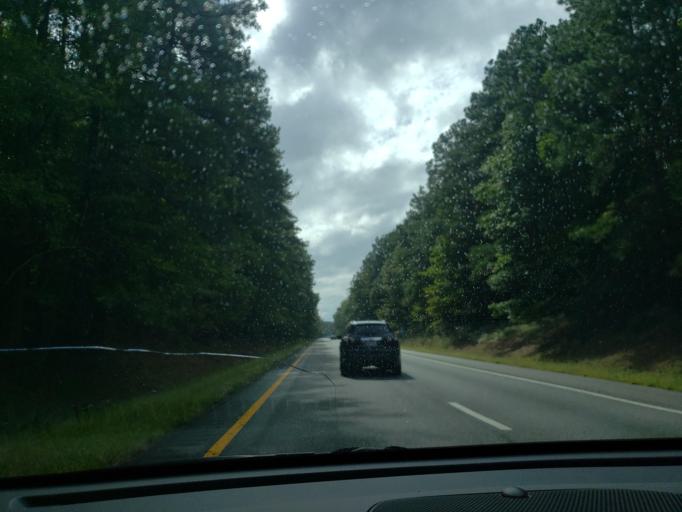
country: US
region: Virginia
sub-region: Brunswick County
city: Lawrenceville
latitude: 36.8898
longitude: -77.8080
